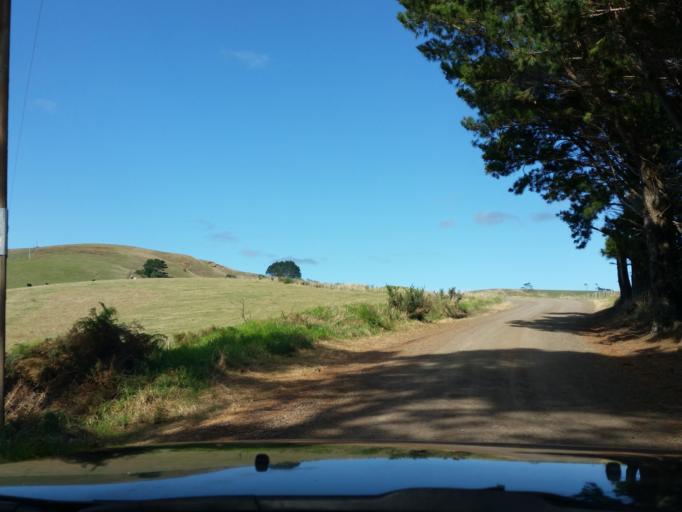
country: NZ
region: Northland
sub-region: Kaipara District
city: Dargaville
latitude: -35.7211
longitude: 173.5636
